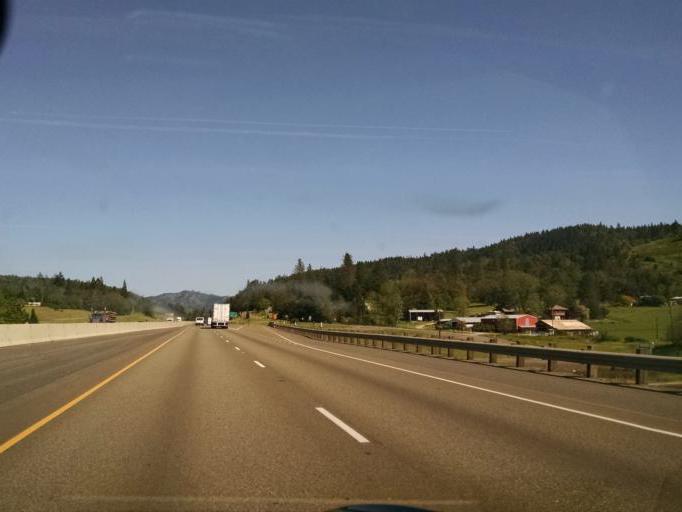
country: US
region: Oregon
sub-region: Douglas County
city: Tri-City
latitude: 42.9478
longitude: -123.3220
